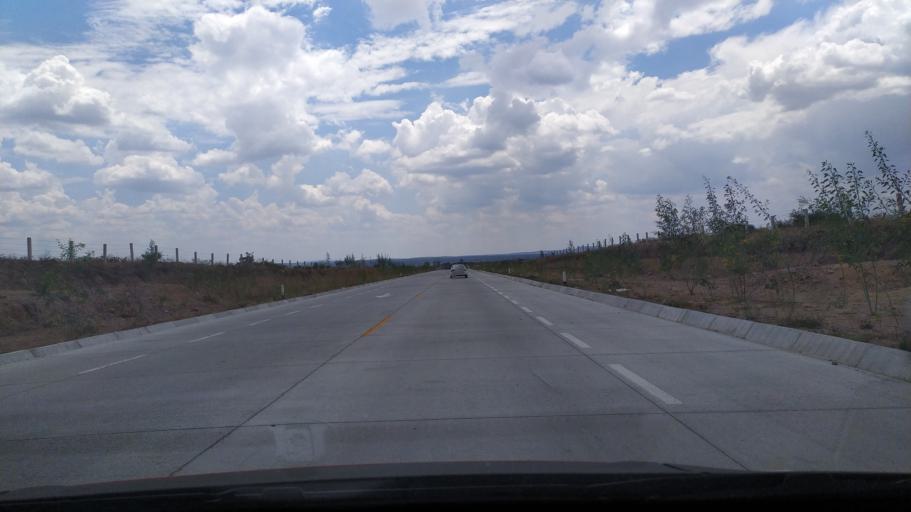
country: MX
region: Guanajuato
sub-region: San Francisco del Rincon
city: Estacion de San Francisco
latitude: 21.0870
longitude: -101.8110
